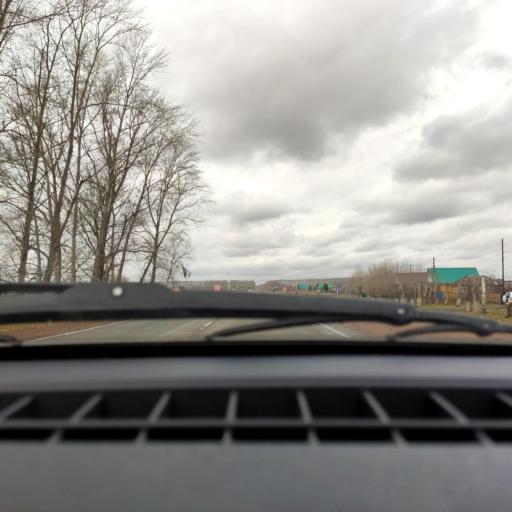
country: RU
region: Bashkortostan
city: Asanovo
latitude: 54.9613
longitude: 55.5490
